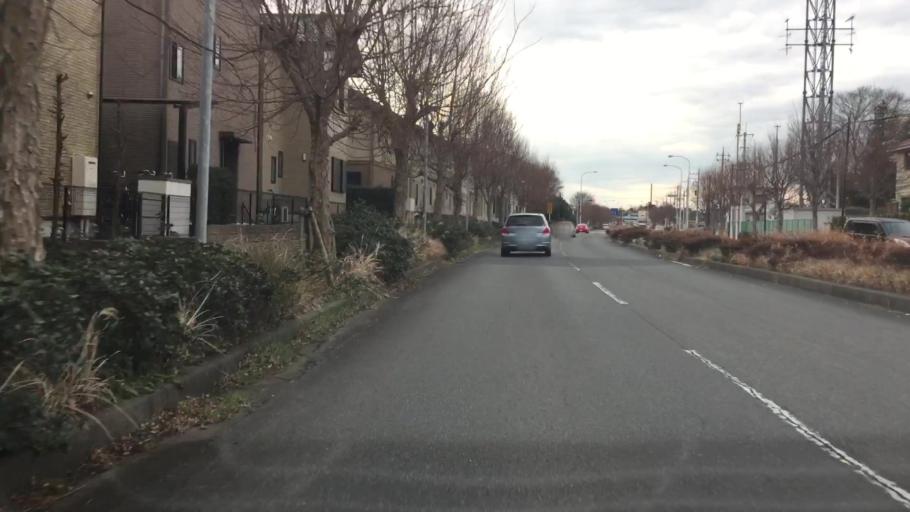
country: JP
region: Chiba
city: Shiroi
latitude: 35.8035
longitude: 140.1037
